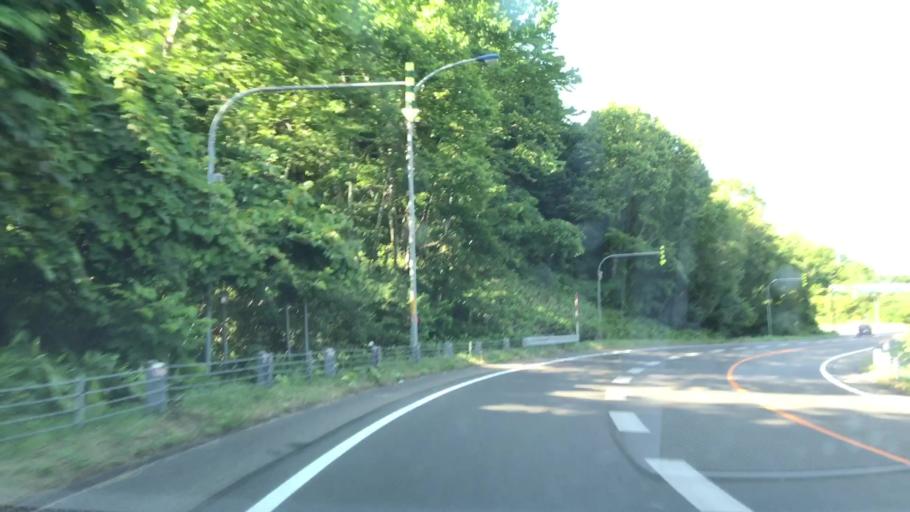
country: JP
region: Hokkaido
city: Shimo-furano
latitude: 42.9017
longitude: 142.4209
